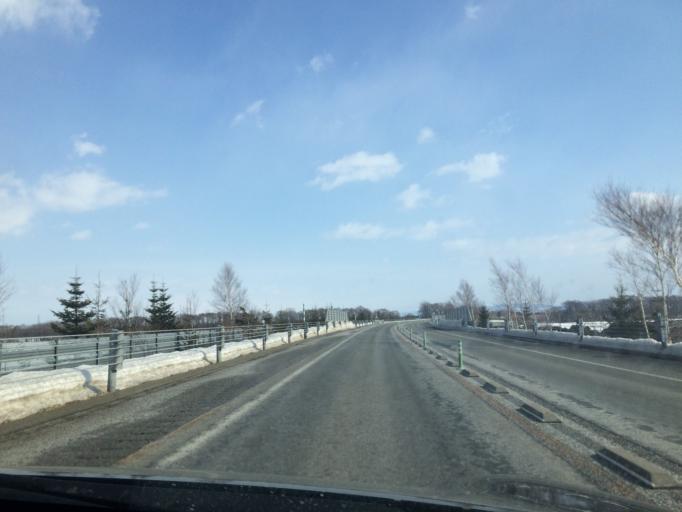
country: JP
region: Hokkaido
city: Chitose
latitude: 42.8798
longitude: 141.6191
